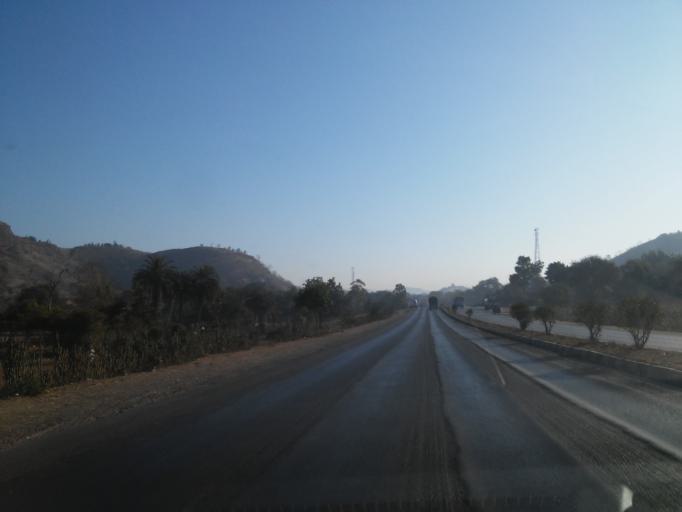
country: IN
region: Rajasthan
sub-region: Dungarpur
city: Dungarpur
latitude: 24.0017
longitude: 73.6475
